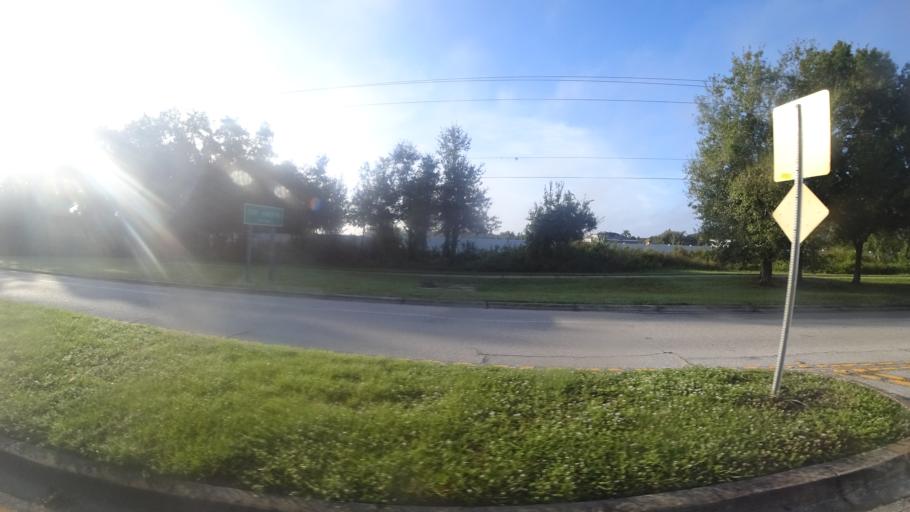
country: US
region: Florida
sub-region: Manatee County
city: Ellenton
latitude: 27.5484
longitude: -82.4270
